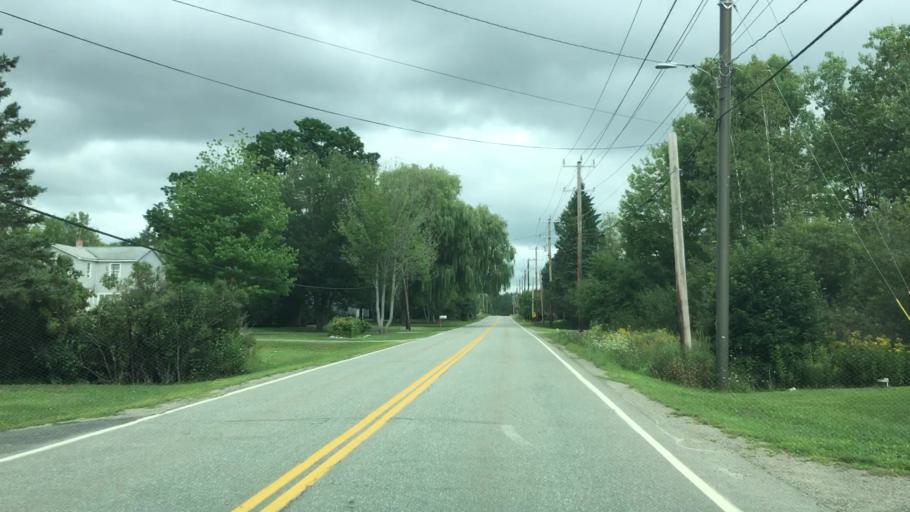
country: US
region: Maine
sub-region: Penobscot County
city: Brewer
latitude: 44.7674
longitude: -68.7662
